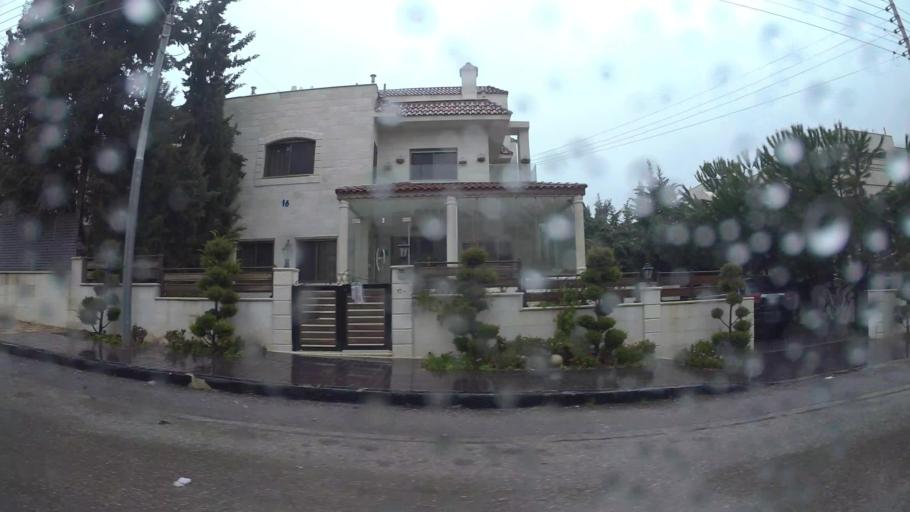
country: JO
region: Amman
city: Wadi as Sir
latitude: 31.9953
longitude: 35.8238
